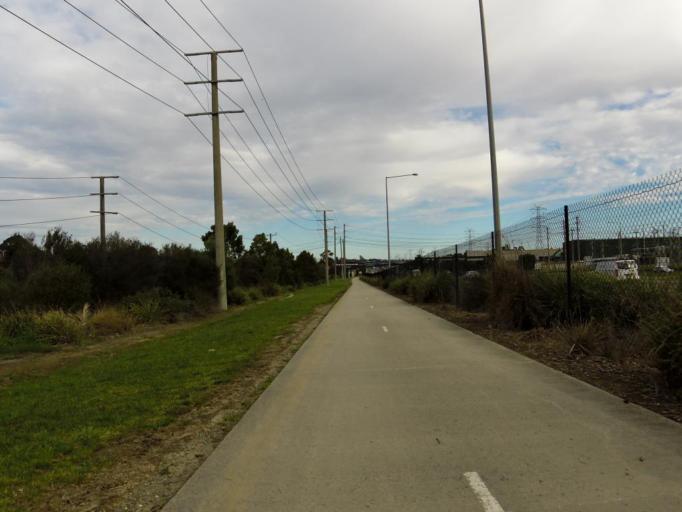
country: AU
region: Victoria
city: Mitcham
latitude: -37.8206
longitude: 145.2176
